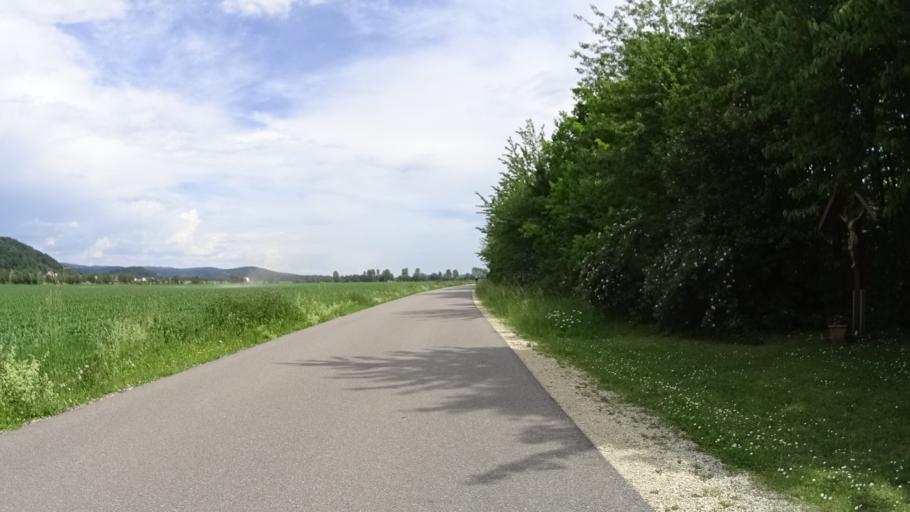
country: DE
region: Bavaria
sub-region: Upper Palatinate
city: Wiesent
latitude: 49.0134
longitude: 12.3244
